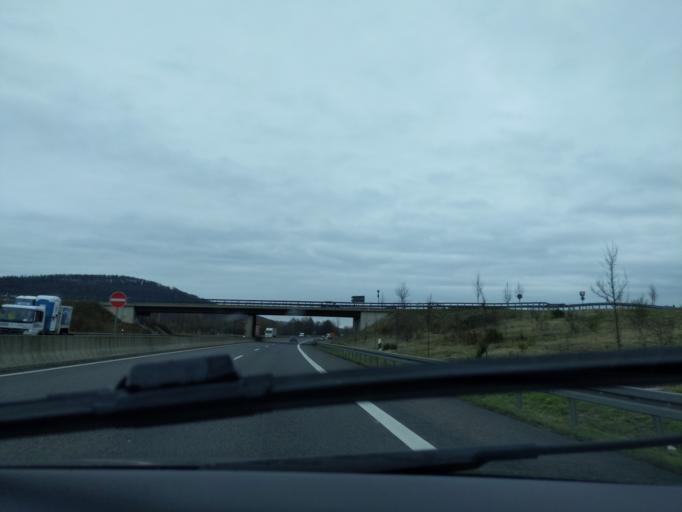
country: DE
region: Hesse
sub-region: Regierungsbezirk Giessen
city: Marburg an der Lahn
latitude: 50.7521
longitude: 8.7408
